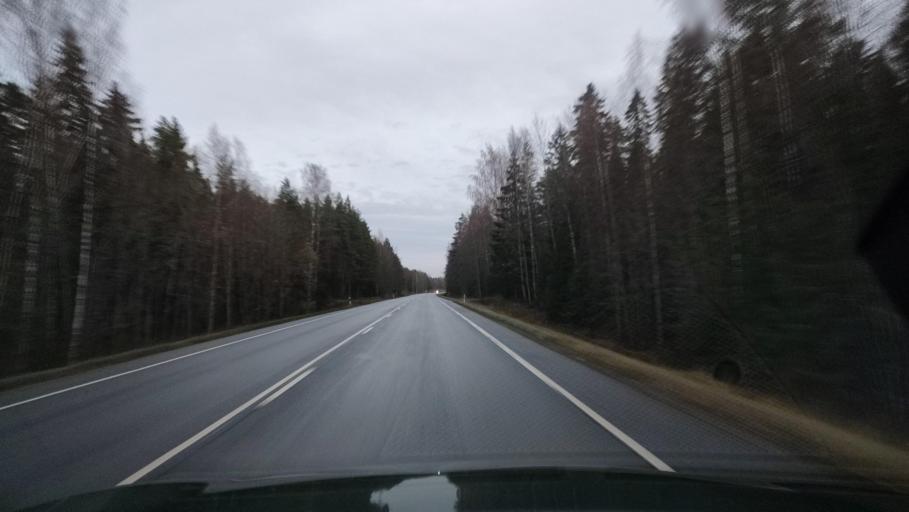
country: FI
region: Ostrobothnia
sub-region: Vaasa
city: Ristinummi
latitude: 63.0145
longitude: 21.7604
